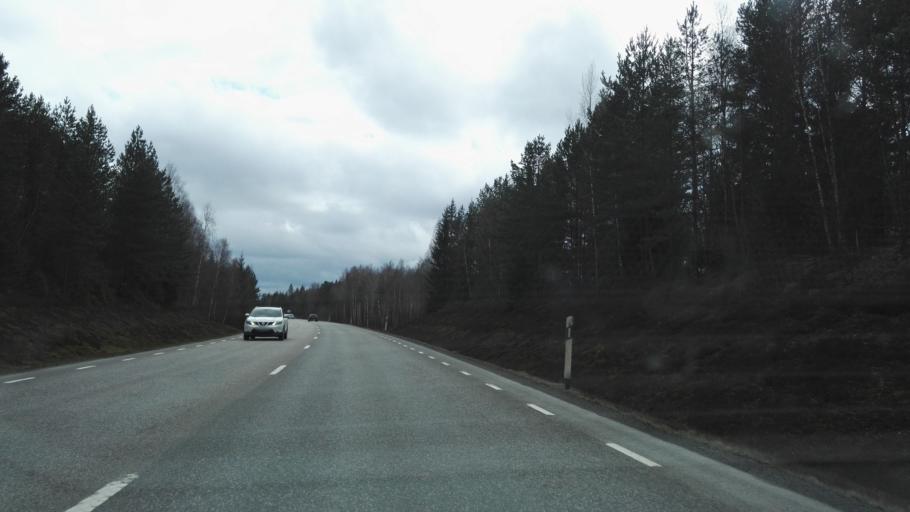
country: SE
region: Kronoberg
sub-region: Almhults Kommun
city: AElmhult
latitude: 56.5742
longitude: 14.1849
